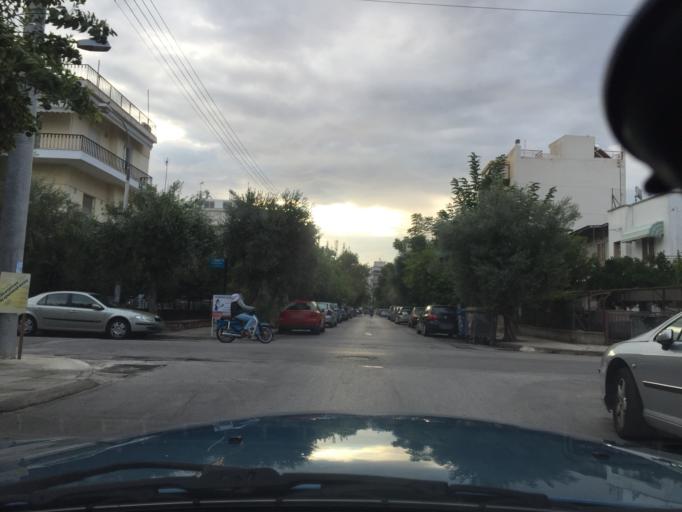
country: GR
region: Attica
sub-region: Nomarchia Athinas
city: Moskhaton
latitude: 37.9470
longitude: 23.6815
